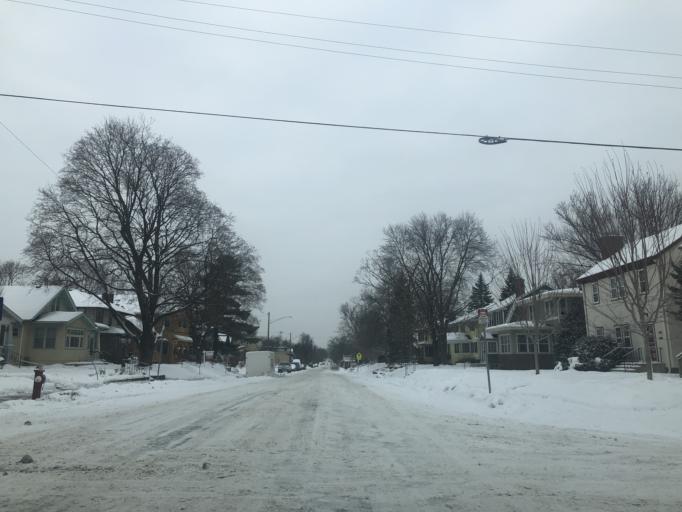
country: US
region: Minnesota
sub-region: Hennepin County
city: Richfield
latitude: 44.9177
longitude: -93.2909
